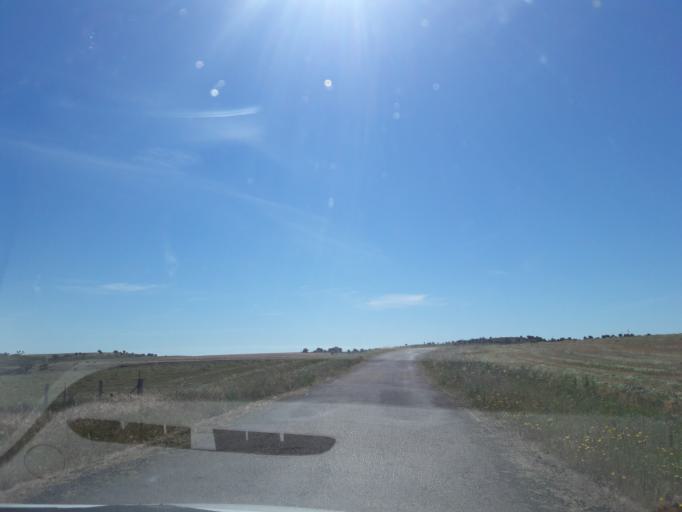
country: ES
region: Castille and Leon
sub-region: Provincia de Salamanca
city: San Pedro del Valle
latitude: 41.0440
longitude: -5.8638
